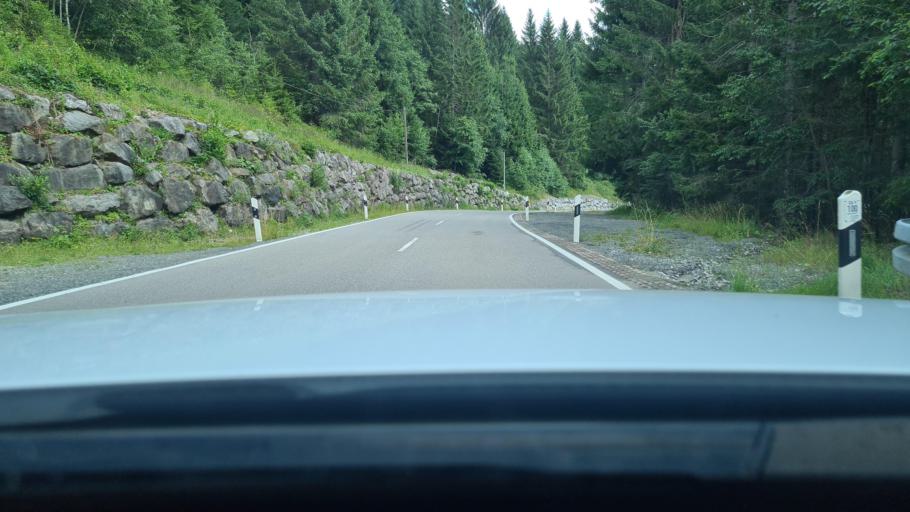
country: DE
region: Bavaria
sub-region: Swabia
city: Obermaiselstein
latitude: 47.4361
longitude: 10.2049
